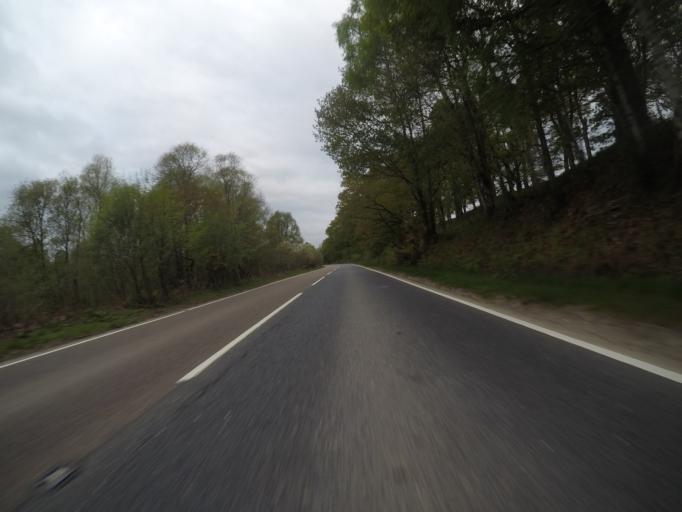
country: GB
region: Scotland
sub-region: Highland
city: Spean Bridge
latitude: 56.8944
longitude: -4.8909
